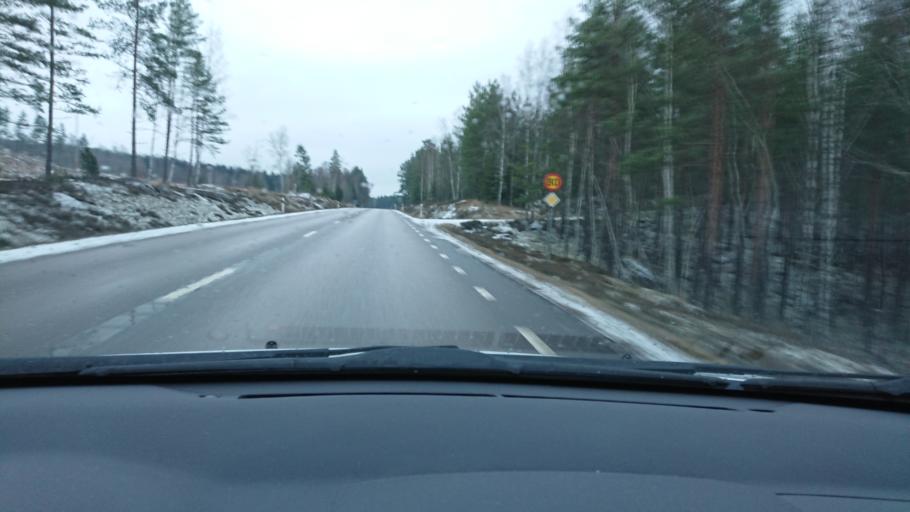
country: SE
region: Kalmar
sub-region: Hultsfreds Kommun
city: Hultsfred
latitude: 57.5351
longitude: 15.8449
